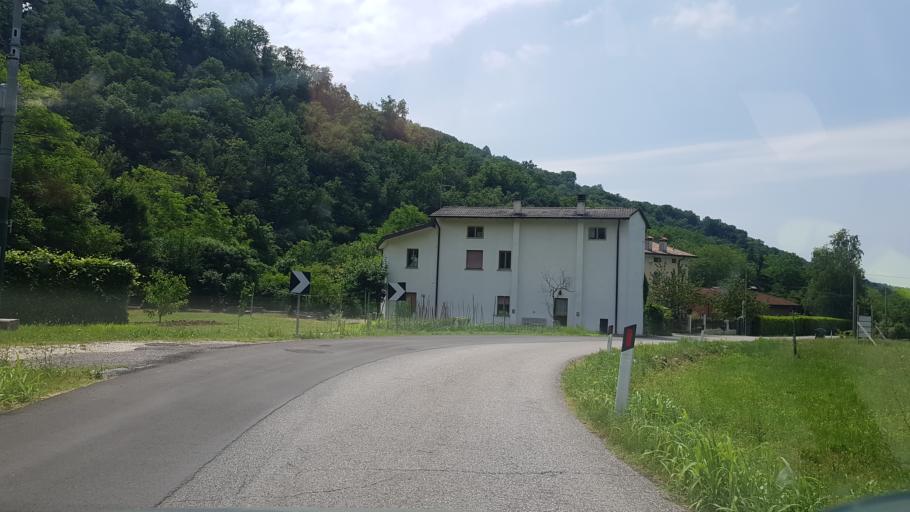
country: IT
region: Friuli Venezia Giulia
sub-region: Provincia di Udine
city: Torreano
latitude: 46.1354
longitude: 13.4382
